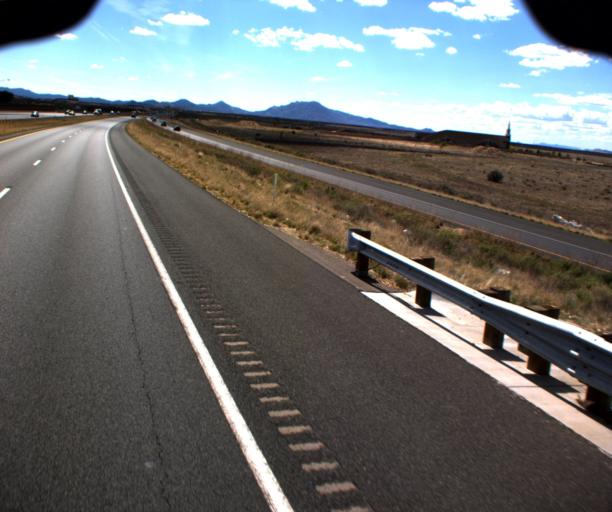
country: US
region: Arizona
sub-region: Yavapai County
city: Prescott Valley
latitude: 34.6359
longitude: -112.3368
